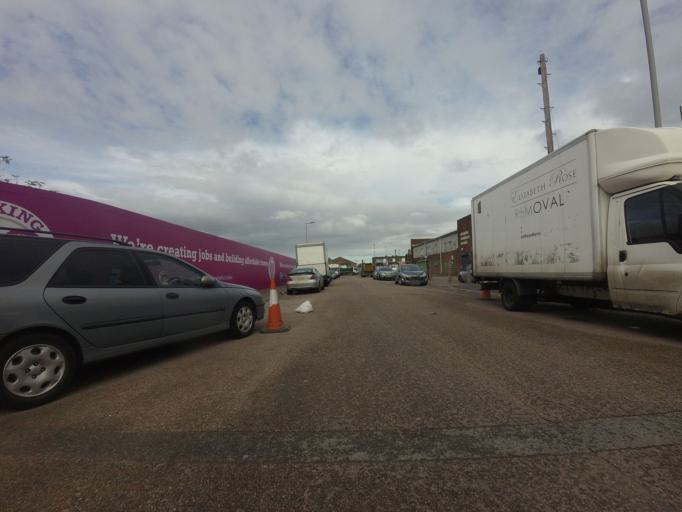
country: GB
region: England
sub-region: Greater London
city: Barking
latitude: 51.5244
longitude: 0.1016
